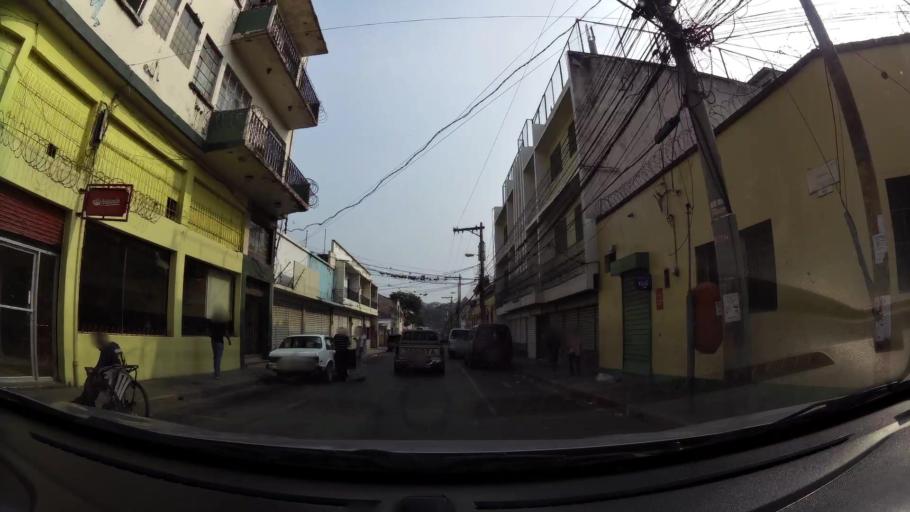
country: HN
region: Francisco Morazan
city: Tegucigalpa
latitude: 14.1071
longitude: -87.2085
